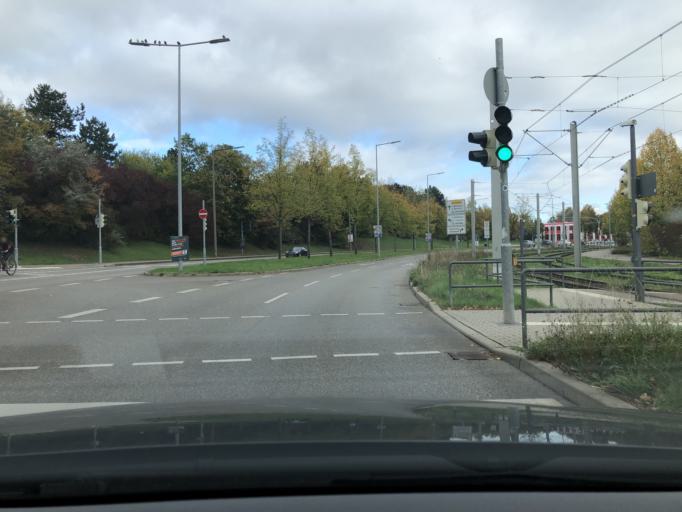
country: DE
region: Baden-Wuerttemberg
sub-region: Regierungsbezirk Stuttgart
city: Stuttgart-Ost
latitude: 48.8166
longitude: 9.2027
